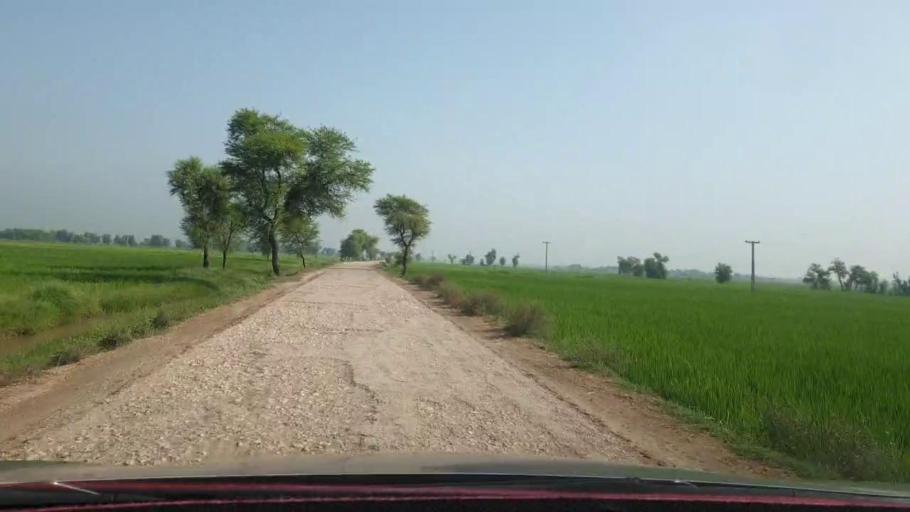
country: PK
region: Sindh
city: Nasirabad
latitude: 27.4872
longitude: 67.9263
